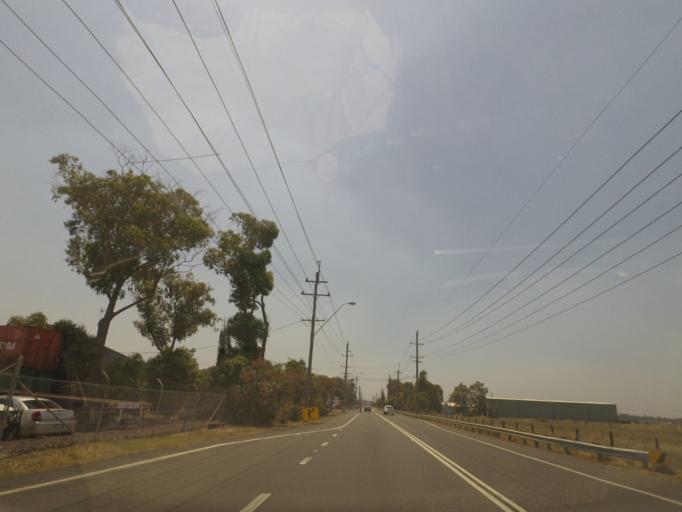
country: AU
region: New South Wales
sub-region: Newcastle
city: Mayfield West
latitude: -32.8260
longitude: 151.7394
